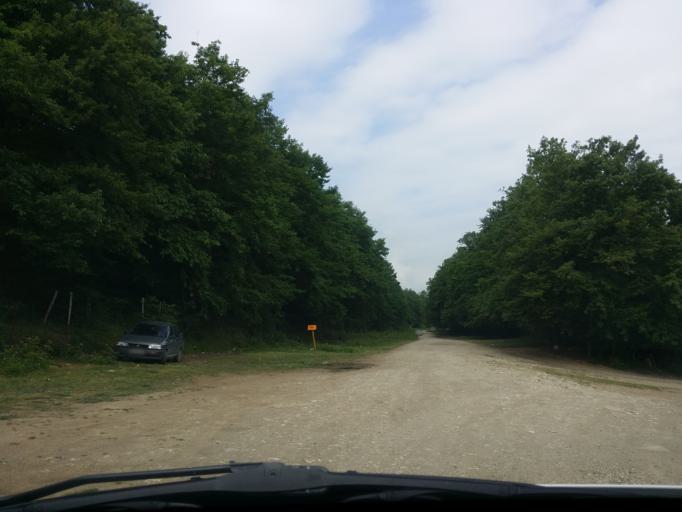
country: IR
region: Mazandaran
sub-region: Nowshahr
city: Nowshahr
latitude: 36.6187
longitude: 51.4953
